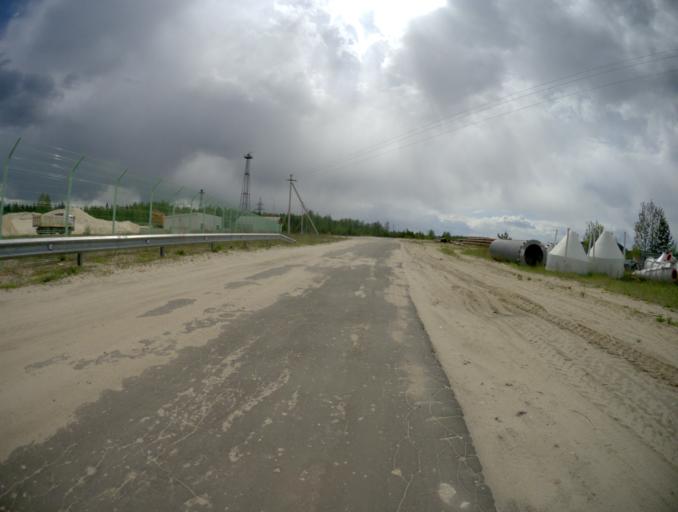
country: RU
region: Vladimir
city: Velikodvorskiy
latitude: 55.2327
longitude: 40.6546
